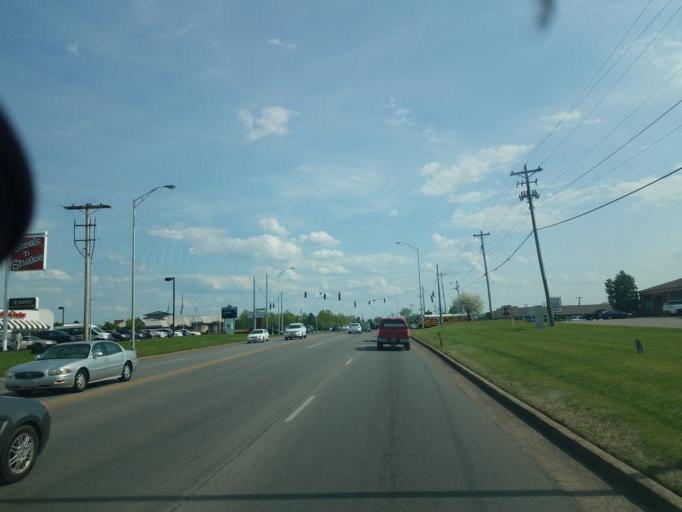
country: US
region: Kentucky
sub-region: Warren County
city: Bowling Green
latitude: 36.9707
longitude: -86.4345
